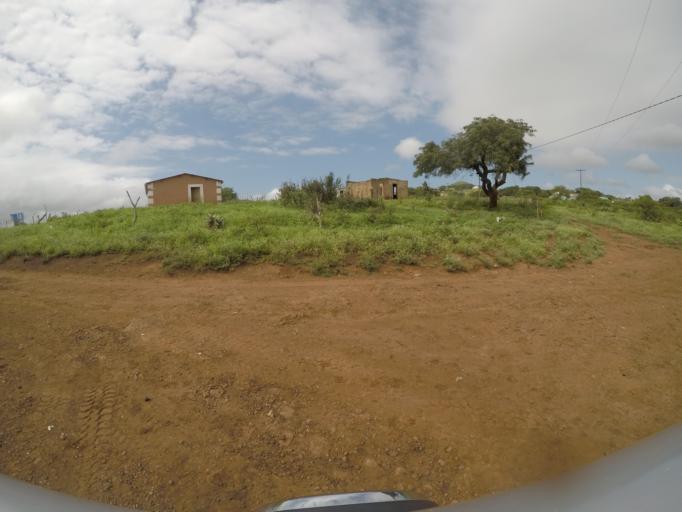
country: ZA
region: KwaZulu-Natal
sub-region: uThungulu District Municipality
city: Empangeni
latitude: -28.6211
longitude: 31.8716
